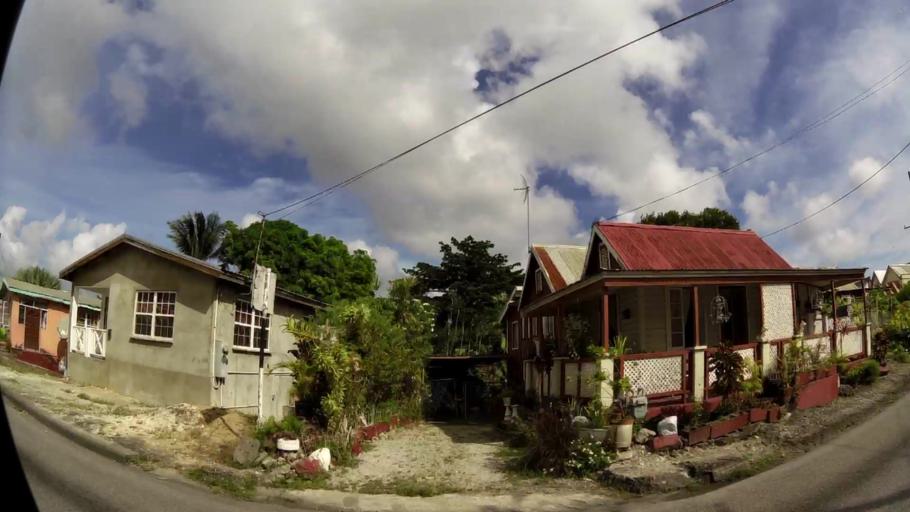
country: BB
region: Saint Michael
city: Bridgetown
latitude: 13.1126
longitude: -59.6030
